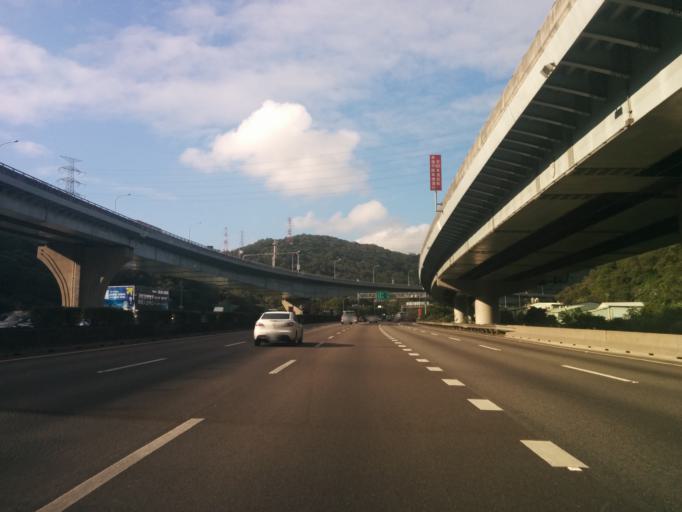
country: TW
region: Taipei
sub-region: Taipei
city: Banqiao
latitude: 25.0574
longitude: 121.4086
